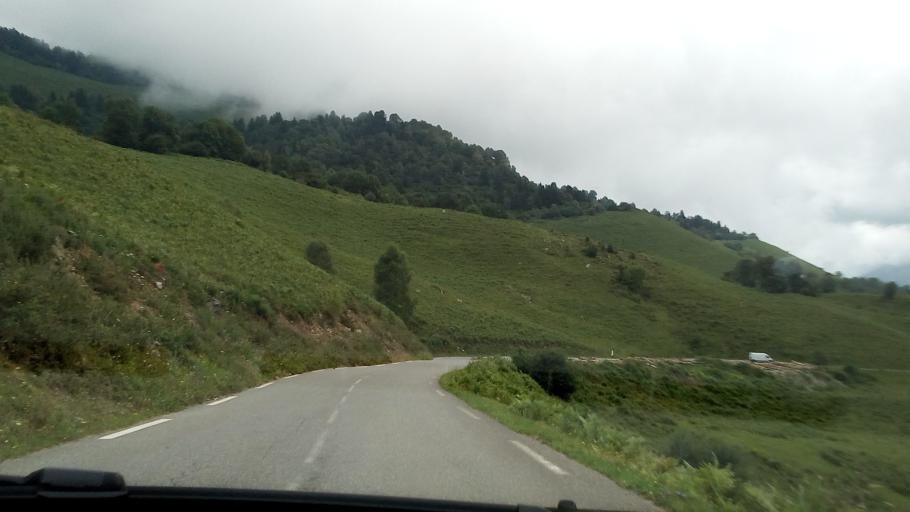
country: FR
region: Aquitaine
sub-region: Departement des Pyrenees-Atlantiques
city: Louvie-Juzon
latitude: 43.0658
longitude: -0.4629
